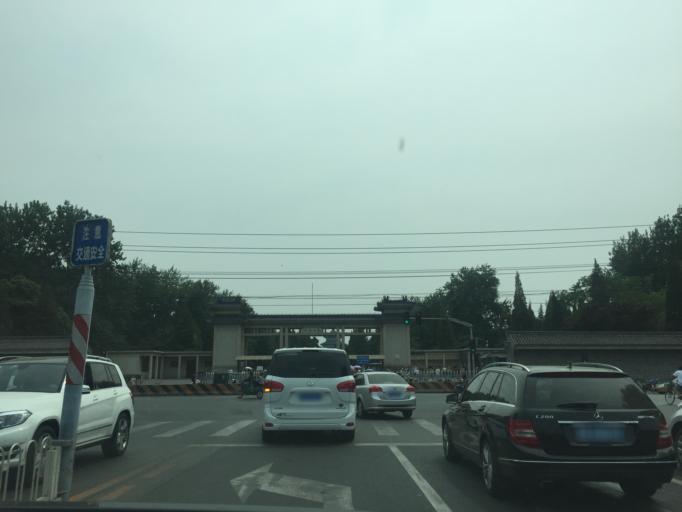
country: CN
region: Beijing
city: Longtan
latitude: 39.8873
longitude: 116.4063
